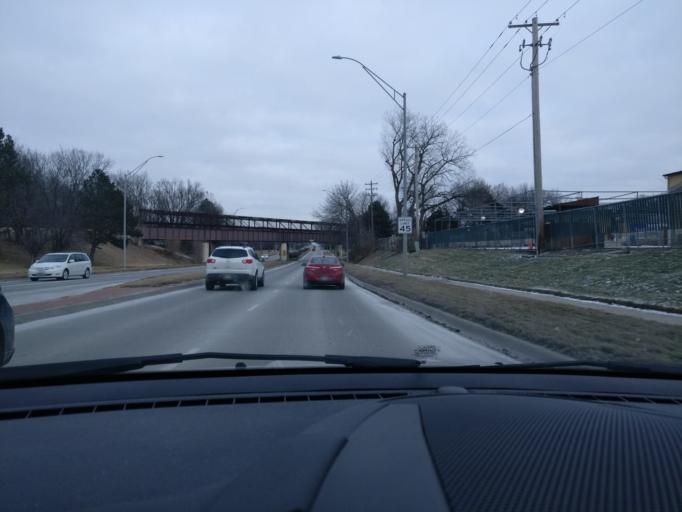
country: US
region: Nebraska
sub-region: Lancaster County
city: Lincoln
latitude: 40.8133
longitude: -96.6225
